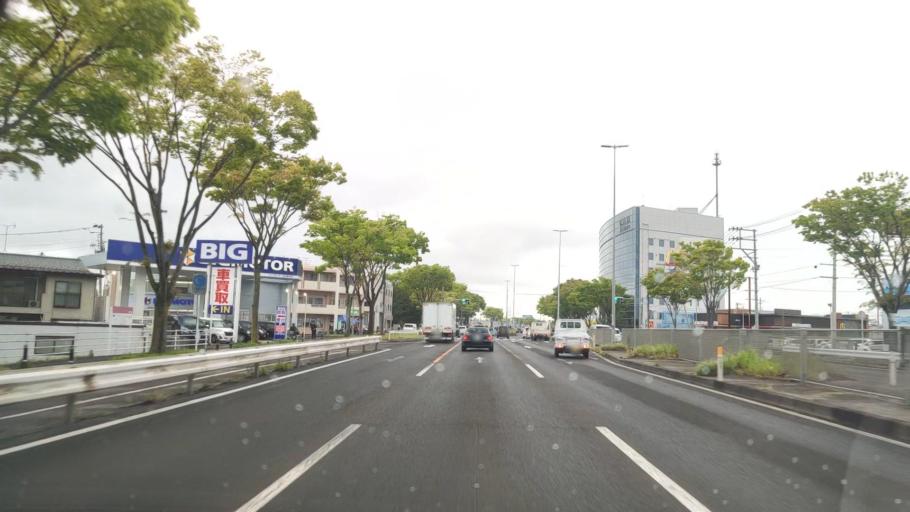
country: JP
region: Miyagi
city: Sendai
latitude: 38.2308
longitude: 140.9065
